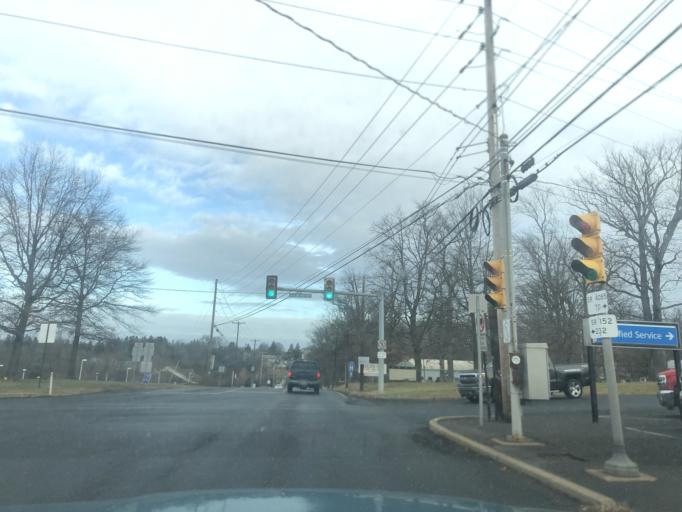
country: US
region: Pennsylvania
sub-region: Bucks County
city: Sellersville
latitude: 40.3449
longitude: -75.3036
